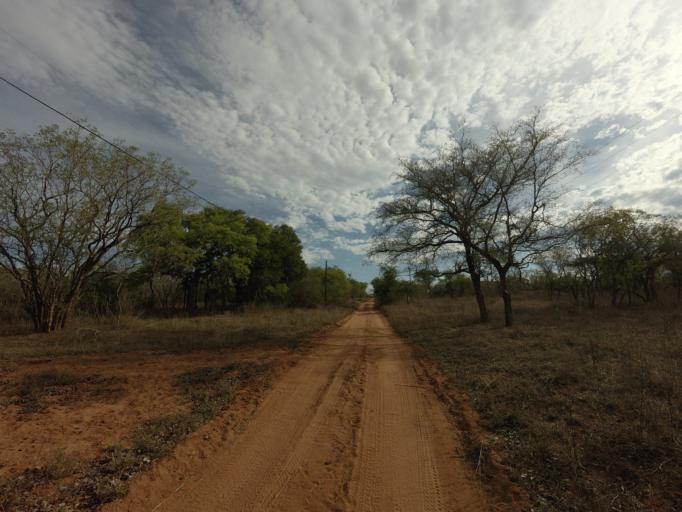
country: ZA
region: Limpopo
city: Thulamahashi
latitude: -24.5277
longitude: 31.1211
